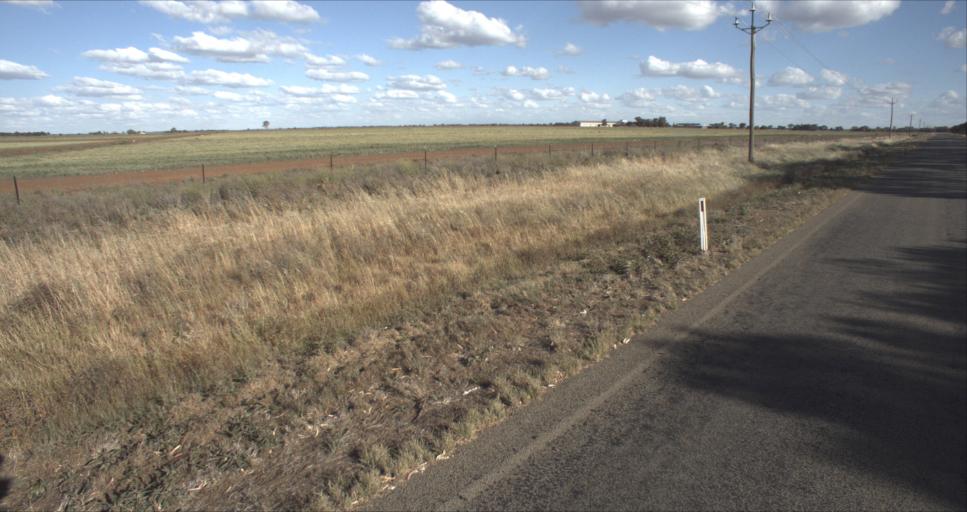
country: AU
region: New South Wales
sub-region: Leeton
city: Leeton
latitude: -34.5424
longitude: 146.2798
